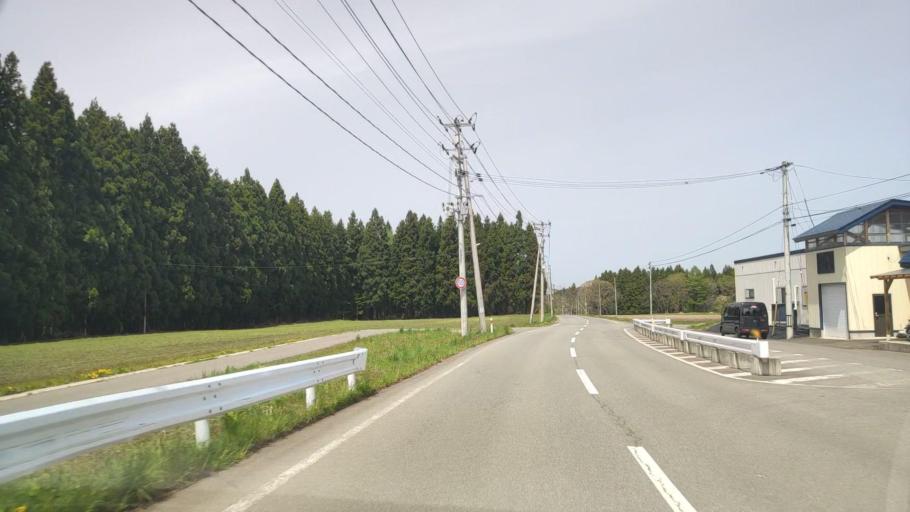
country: JP
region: Aomori
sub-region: Misawa Shi
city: Inuotose
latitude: 40.7253
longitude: 141.1412
